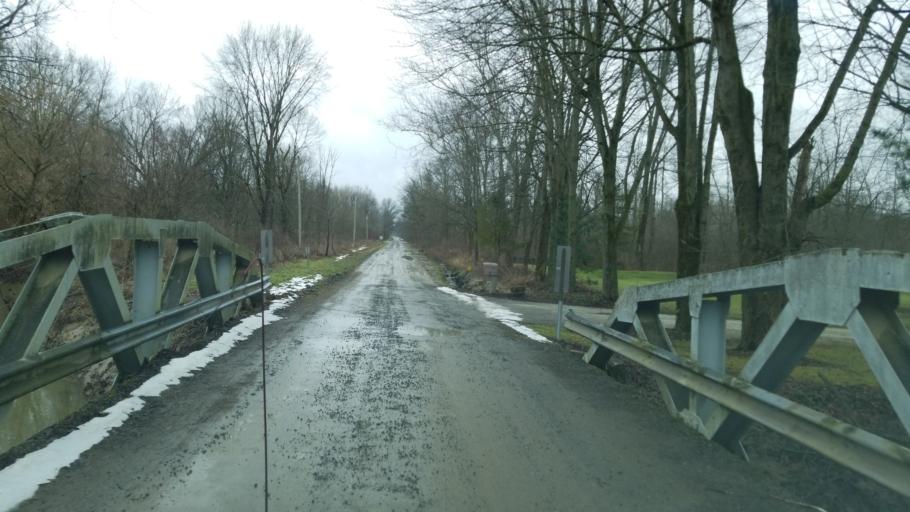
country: US
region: Ohio
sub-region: Ashtabula County
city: Orwell
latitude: 41.4485
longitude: -80.9348
